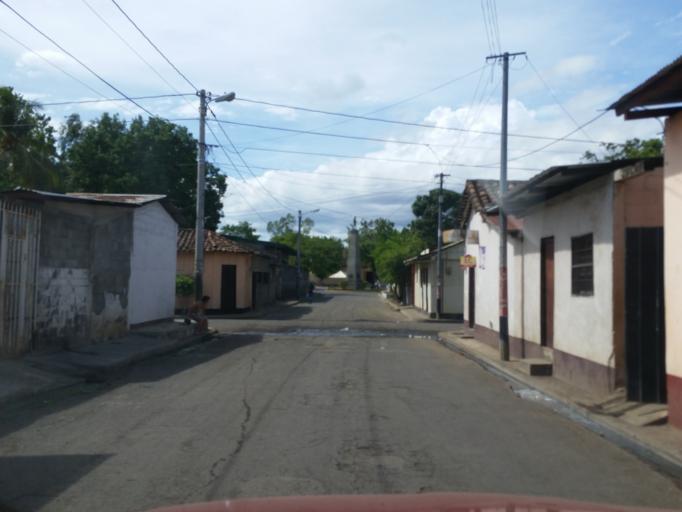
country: NI
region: Masaya
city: Nindiri
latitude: 12.0016
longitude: -86.1199
